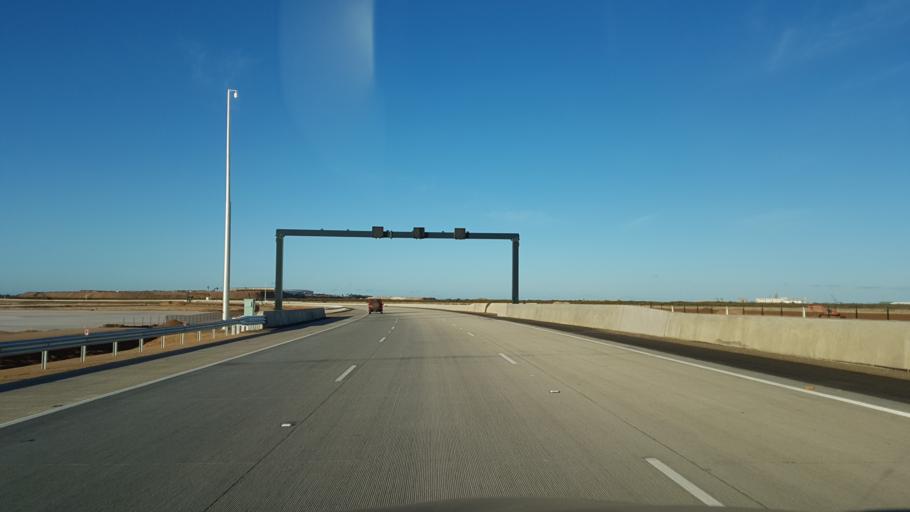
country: AU
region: South Australia
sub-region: Port Adelaide Enfield
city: Enfield
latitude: -34.8108
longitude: 138.5652
